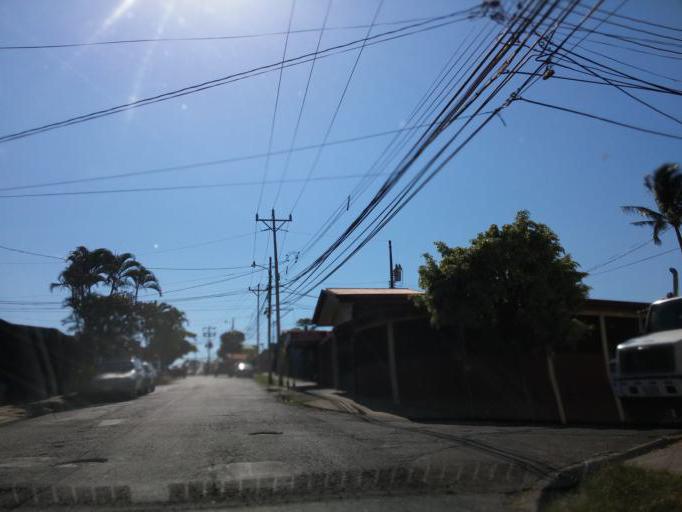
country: CR
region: Alajuela
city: Alajuela
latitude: 10.0137
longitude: -84.2017
